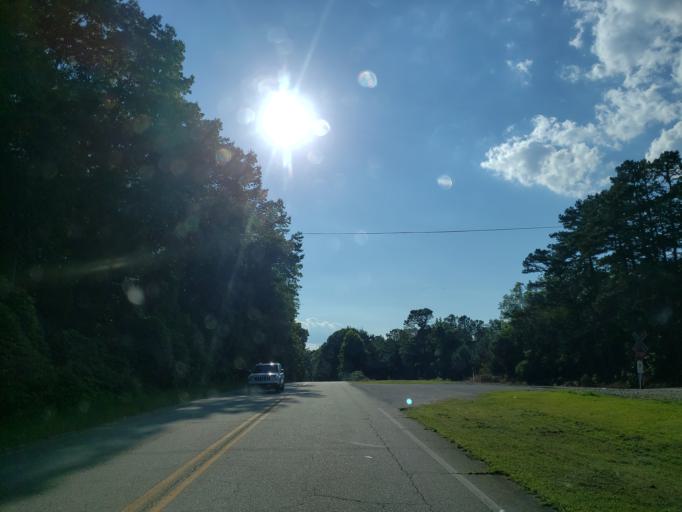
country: US
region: Georgia
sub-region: Haralson County
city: Buchanan
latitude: 33.7868
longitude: -85.1695
